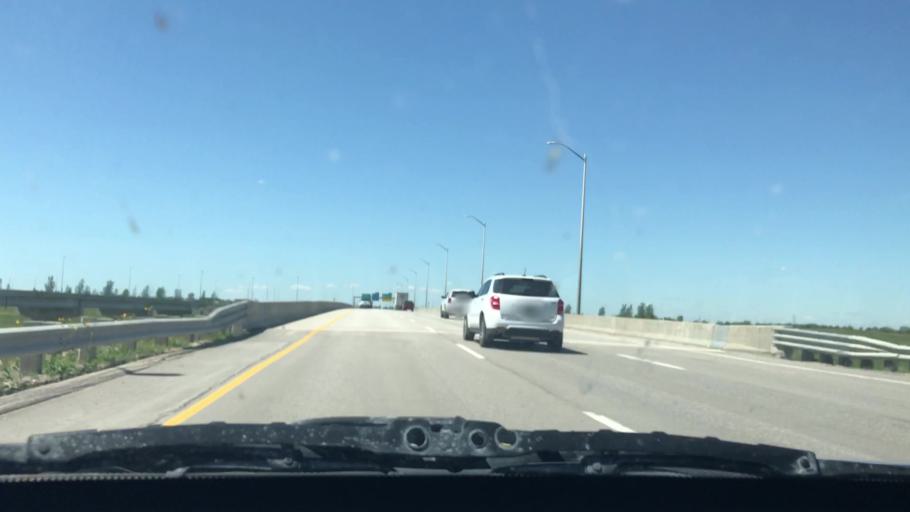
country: CA
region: Manitoba
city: Winnipeg
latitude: 49.8307
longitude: -96.9529
